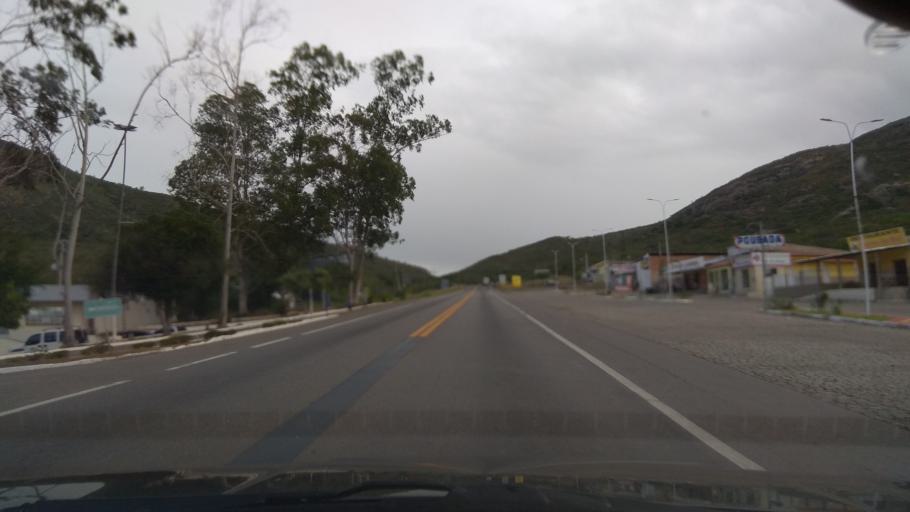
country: BR
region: Bahia
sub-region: Amargosa
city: Amargosa
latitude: -12.8785
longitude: -39.8577
